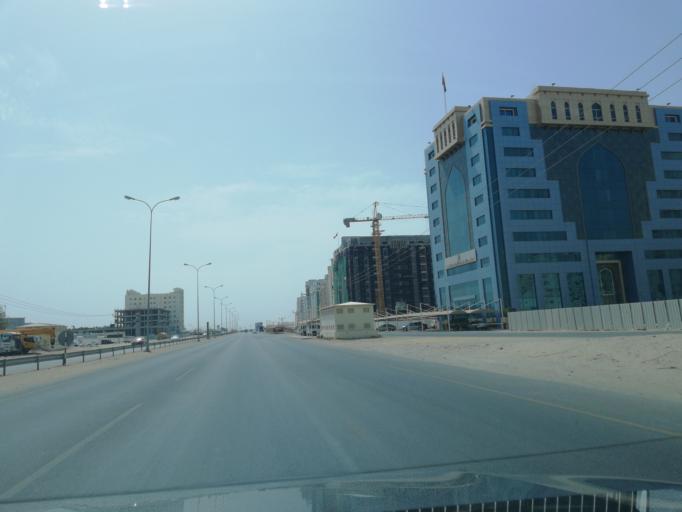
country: OM
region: Muhafazat Masqat
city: Bawshar
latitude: 23.5828
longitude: 58.3719
